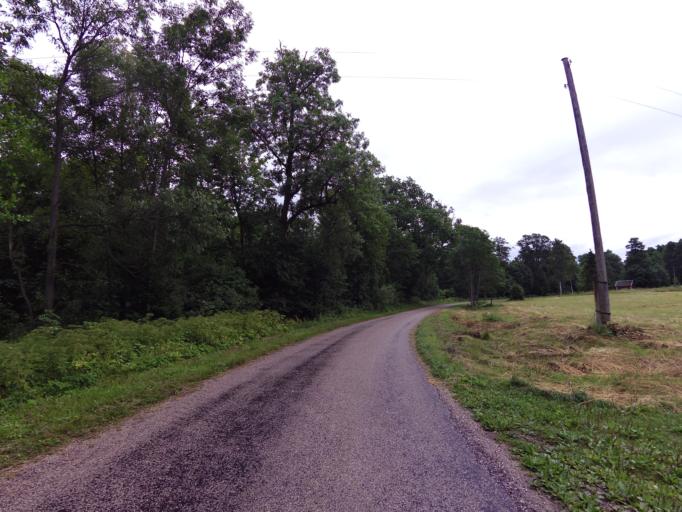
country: EE
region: Laeaene
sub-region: Vormsi vald
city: Hullo
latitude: 59.0177
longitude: 23.3413
